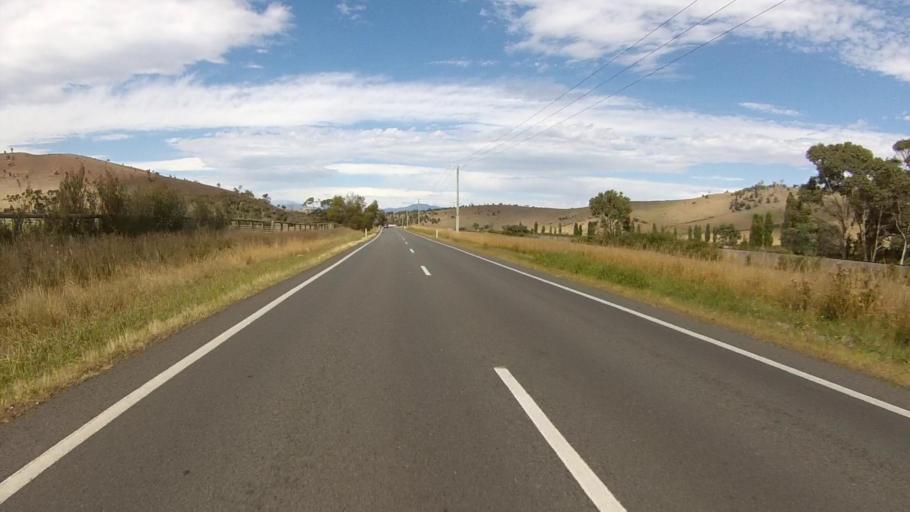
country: AU
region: Tasmania
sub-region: Brighton
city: Old Beach
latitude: -42.6731
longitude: 147.3606
